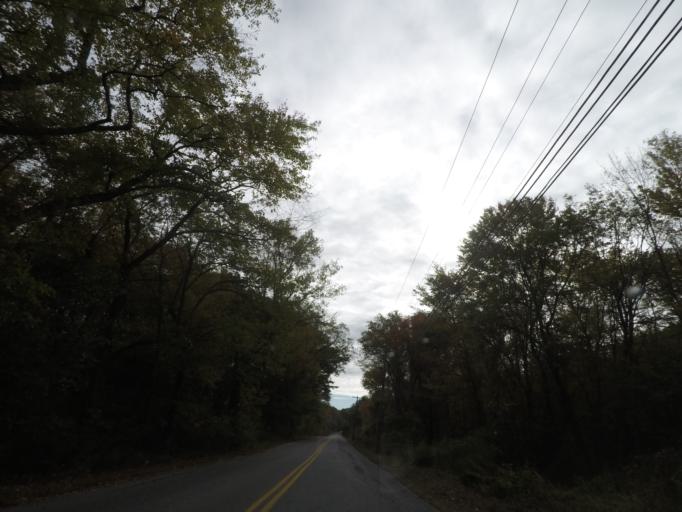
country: US
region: Connecticut
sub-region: Windham County
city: Thompson
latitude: 41.9561
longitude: -71.8568
